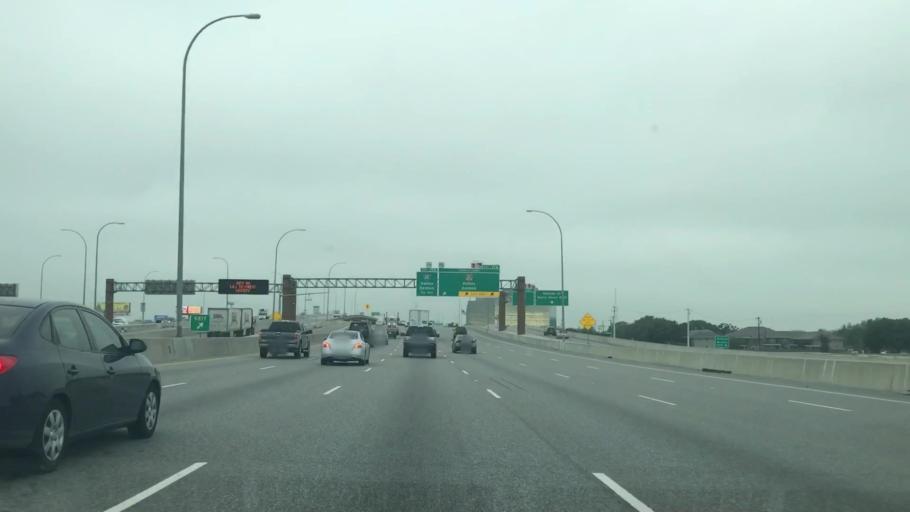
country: US
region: Texas
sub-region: Dallas County
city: Farmers Branch
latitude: 32.9121
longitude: -96.8785
